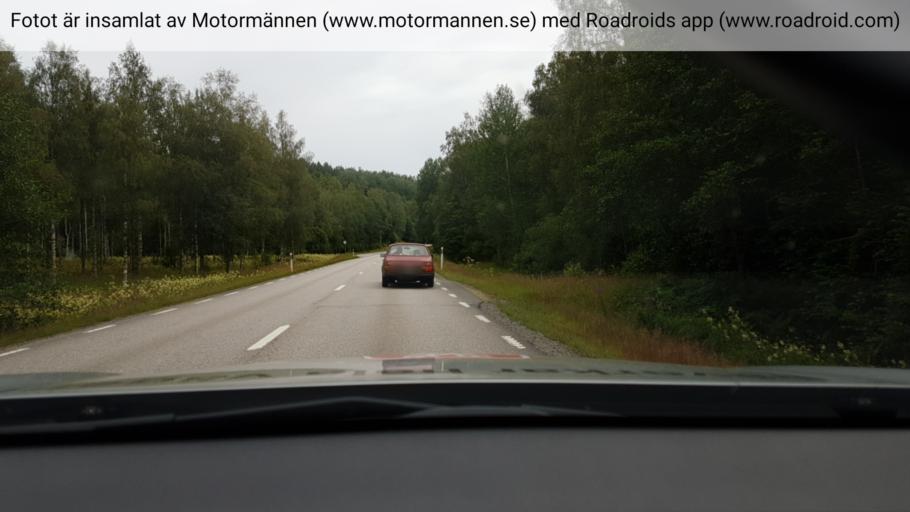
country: SE
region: Vaestra Goetaland
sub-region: Bengtsfors Kommun
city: Dals Langed
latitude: 58.8810
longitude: 12.2126
